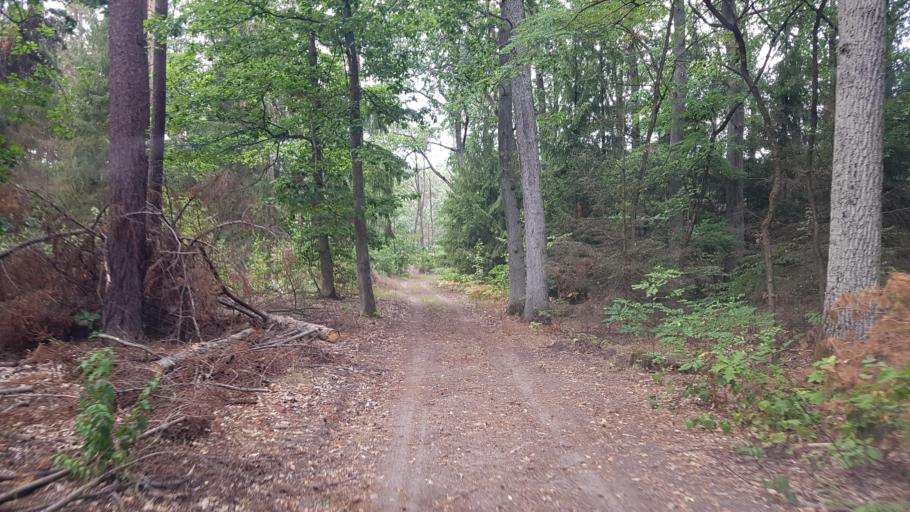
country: DE
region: Brandenburg
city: Bronkow
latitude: 51.7085
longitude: 13.9187
